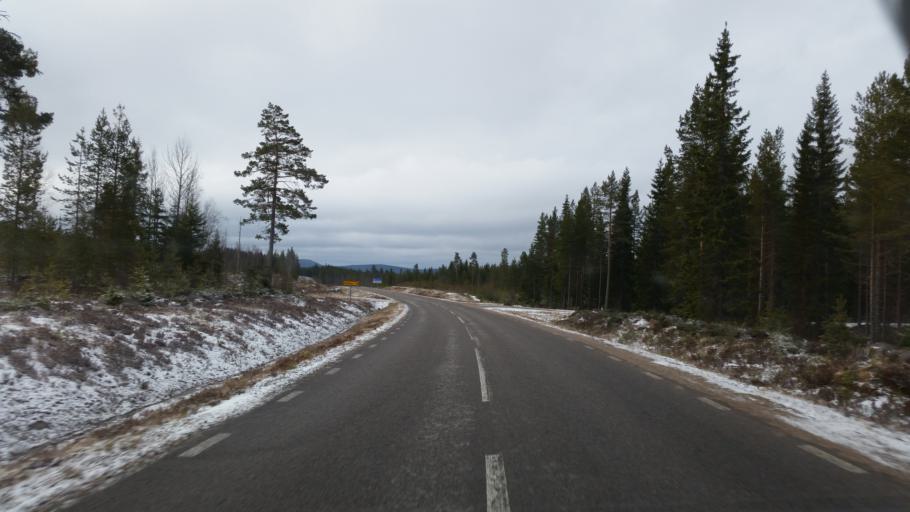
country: SE
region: Gaevleborg
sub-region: Ljusdals Kommun
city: Farila
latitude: 61.6110
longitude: 15.5414
